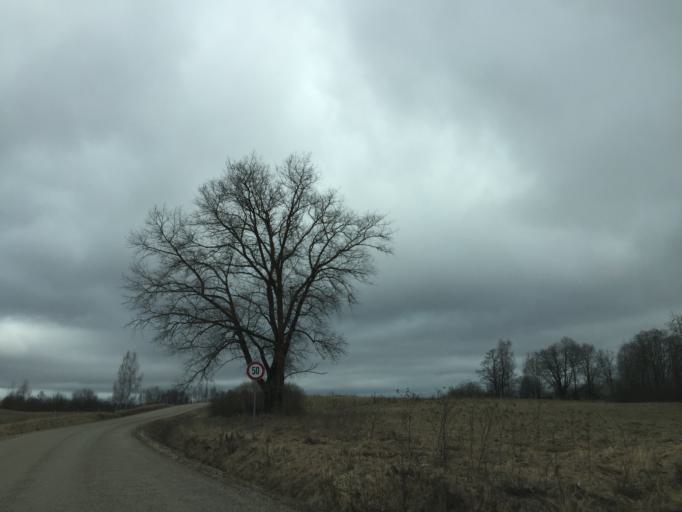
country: LV
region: Ilukste
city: Ilukste
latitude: 56.0390
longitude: 26.2026
